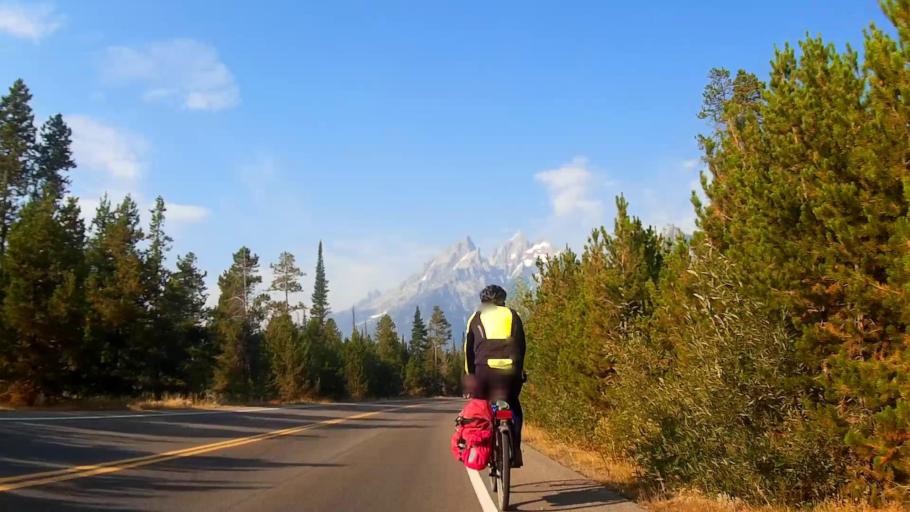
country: US
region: Wyoming
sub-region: Teton County
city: Moose Wilson Road
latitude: 43.7926
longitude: -110.7077
